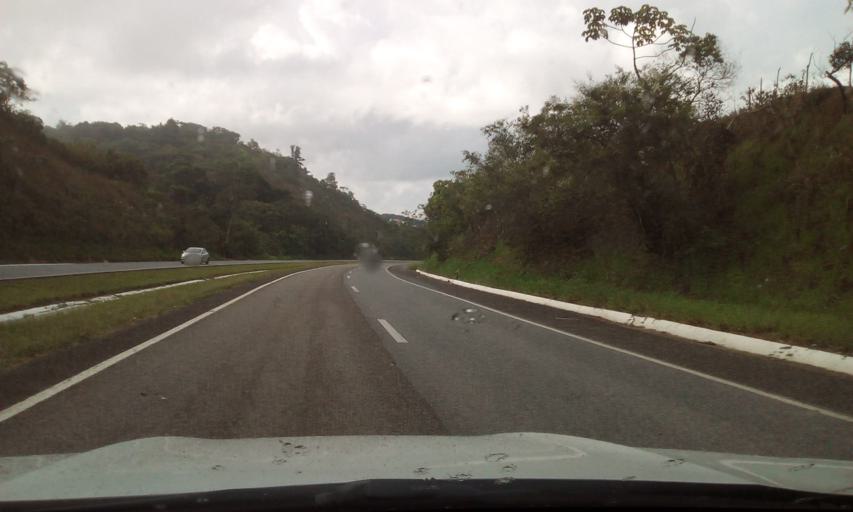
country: BR
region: Pernambuco
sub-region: Cabo De Santo Agostinho
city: Cabo
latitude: -8.2743
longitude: -35.0539
